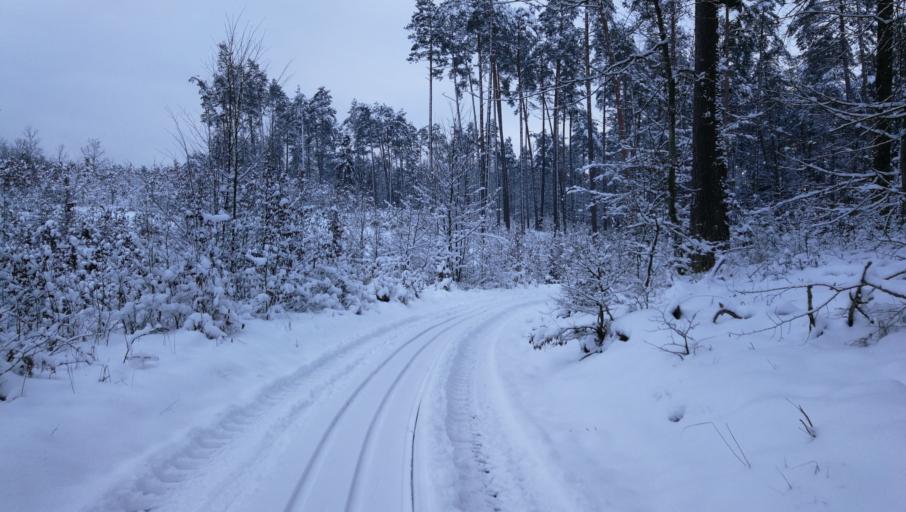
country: PL
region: Kujawsko-Pomorskie
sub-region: Powiat brodnicki
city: Gorzno
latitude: 53.2078
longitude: 19.6973
